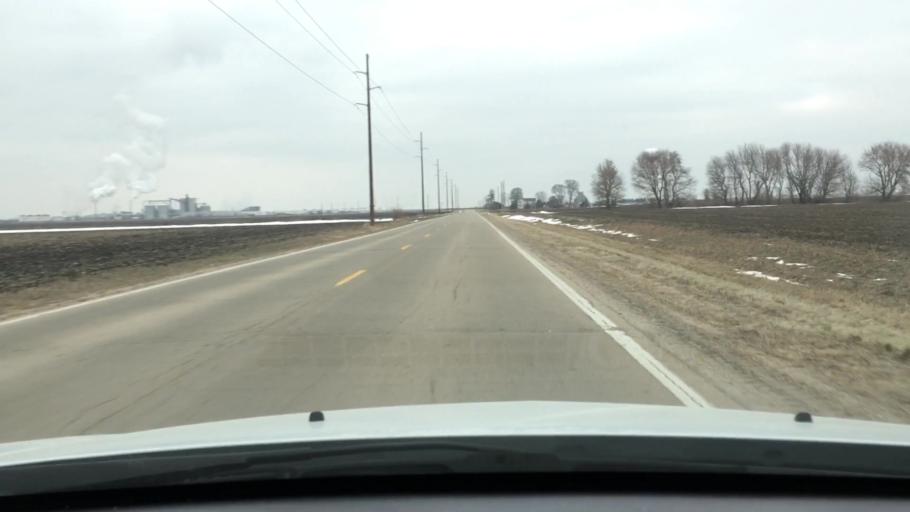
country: US
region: Illinois
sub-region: Ogle County
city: Rochelle
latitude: 41.8746
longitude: -89.0250
